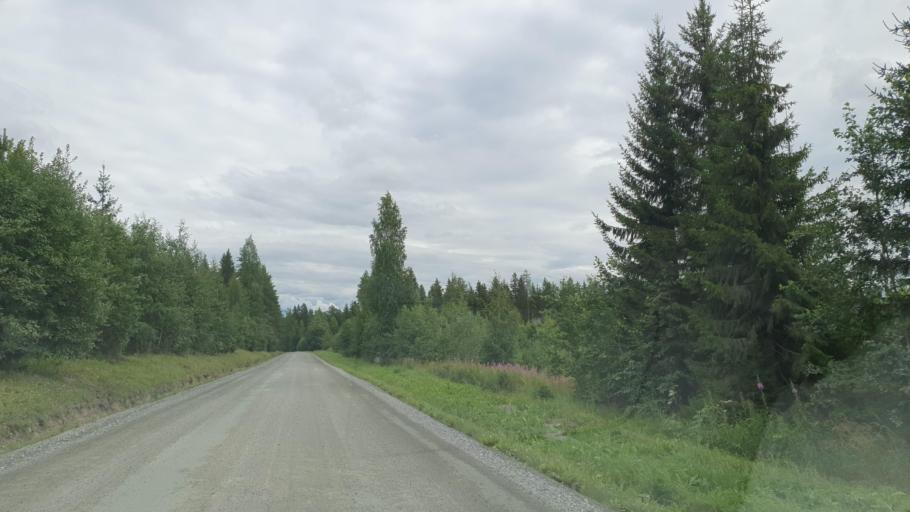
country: FI
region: Northern Savo
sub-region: Ylae-Savo
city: Iisalmi
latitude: 63.5171
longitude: 27.1064
